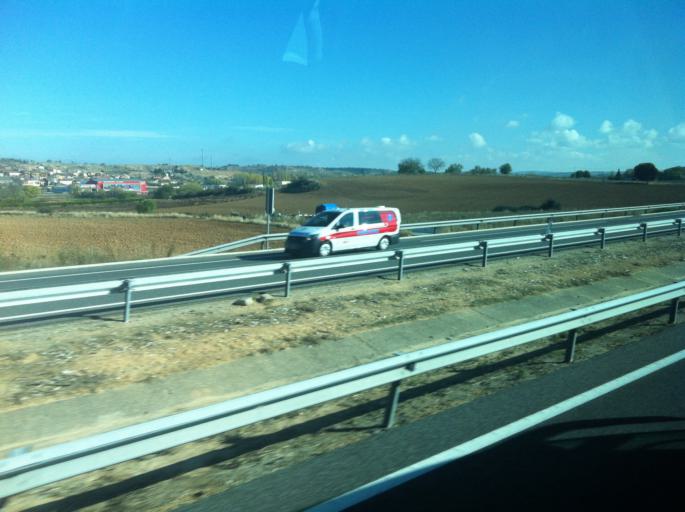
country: ES
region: Castille and Leon
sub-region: Provincia de Burgos
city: Fuentespina
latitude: 41.6304
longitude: -3.6960
